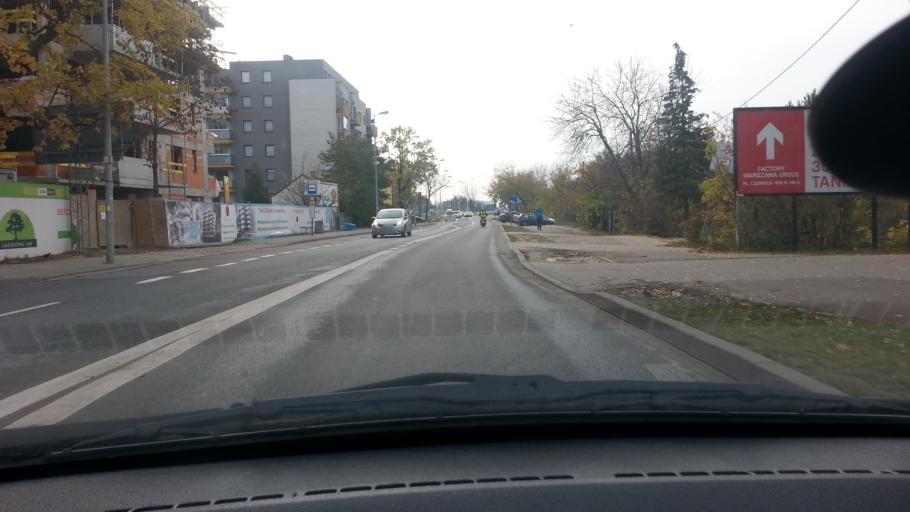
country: PL
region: Masovian Voivodeship
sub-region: Warszawa
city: Bemowo
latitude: 52.2432
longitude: 20.8971
